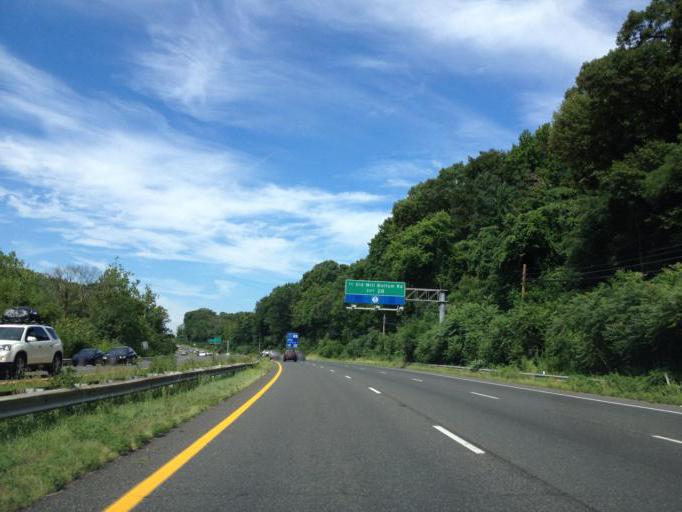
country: US
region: Maryland
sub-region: Anne Arundel County
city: Cape Saint Claire
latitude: 39.0278
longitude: -76.4616
